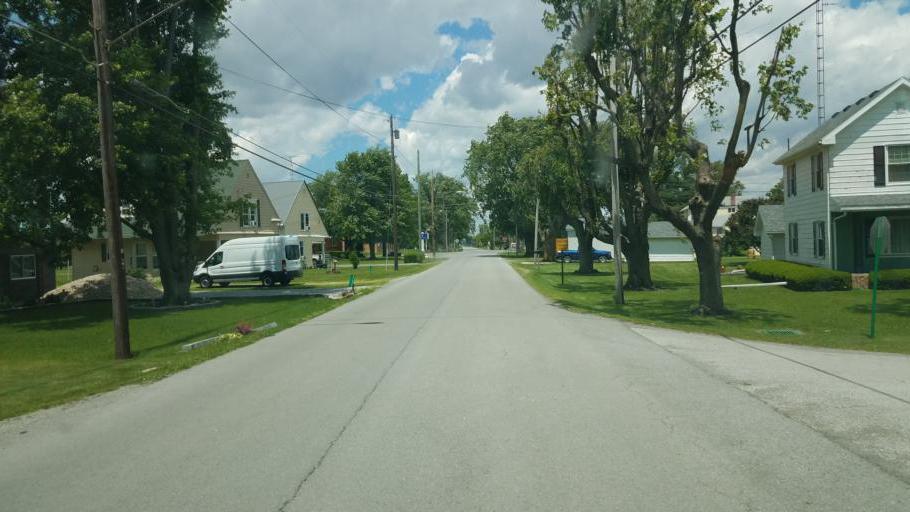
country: US
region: Ohio
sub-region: Wyandot County
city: Upper Sandusky
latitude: 40.7370
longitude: -83.2532
